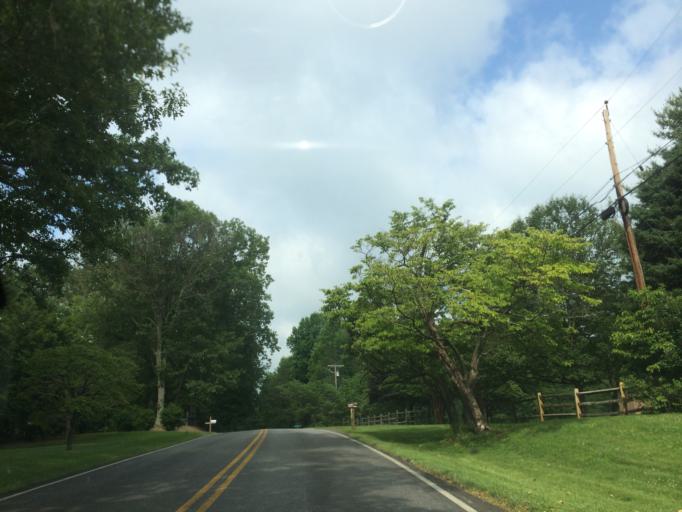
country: US
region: Maryland
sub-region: Howard County
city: Highland
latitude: 39.1980
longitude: -76.9974
